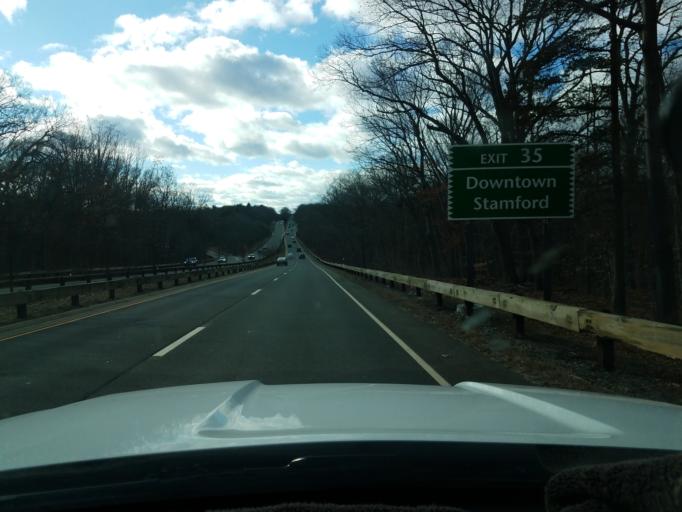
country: US
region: Connecticut
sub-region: Fairfield County
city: North Stamford
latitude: 41.1121
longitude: -73.5492
